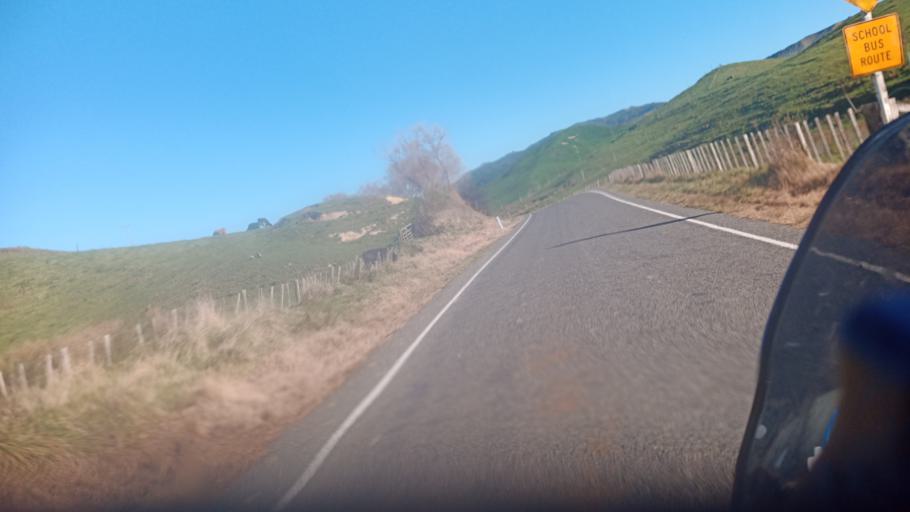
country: NZ
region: Gisborne
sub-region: Gisborne District
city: Gisborne
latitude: -38.5768
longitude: 177.5670
